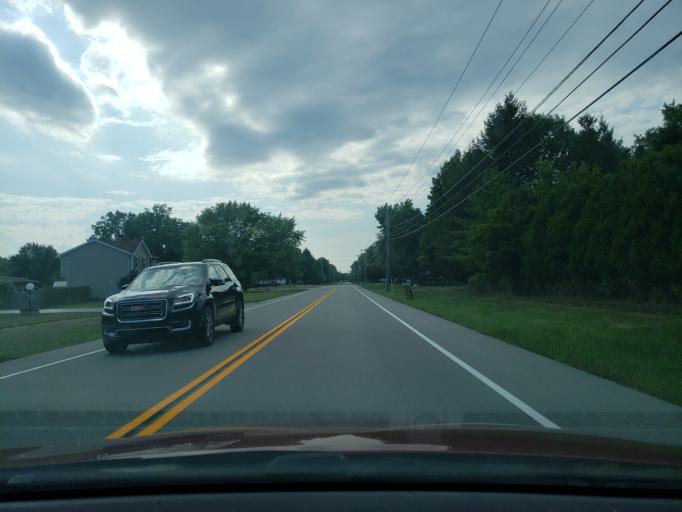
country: US
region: New York
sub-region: Monroe County
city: Greece
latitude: 43.2788
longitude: -77.7081
